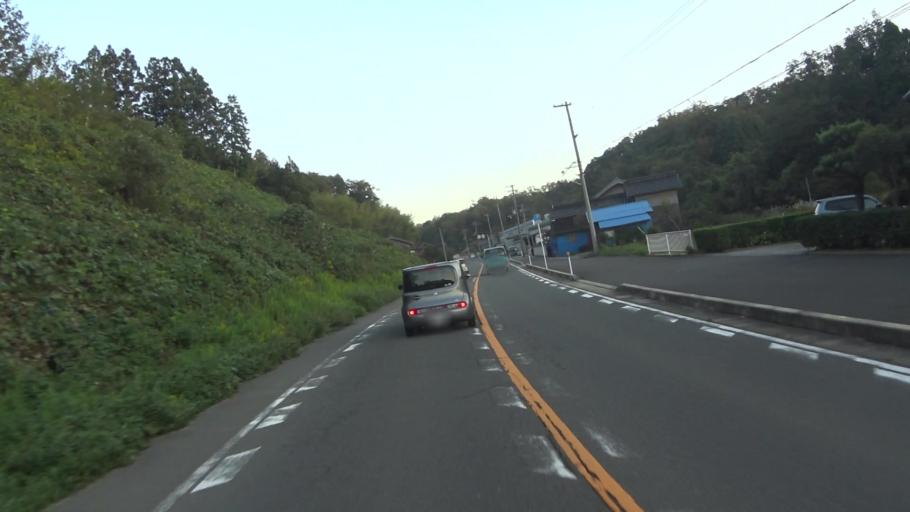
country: JP
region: Kyoto
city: Miyazu
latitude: 35.6482
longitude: 135.0429
